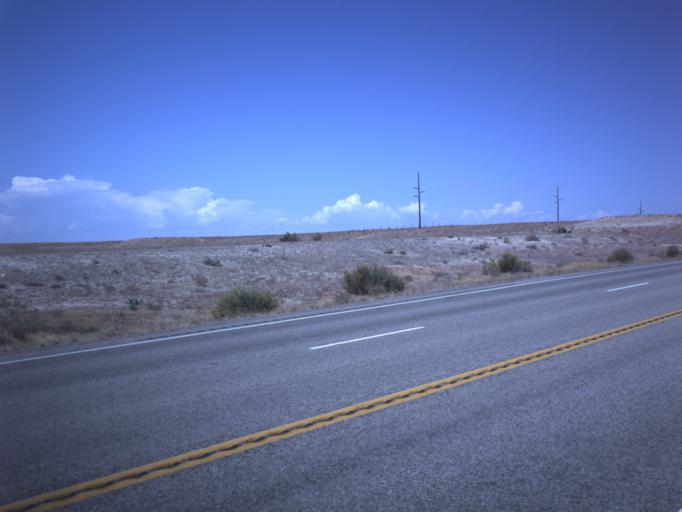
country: US
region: Utah
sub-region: Grand County
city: Moab
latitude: 38.8521
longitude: -109.8018
